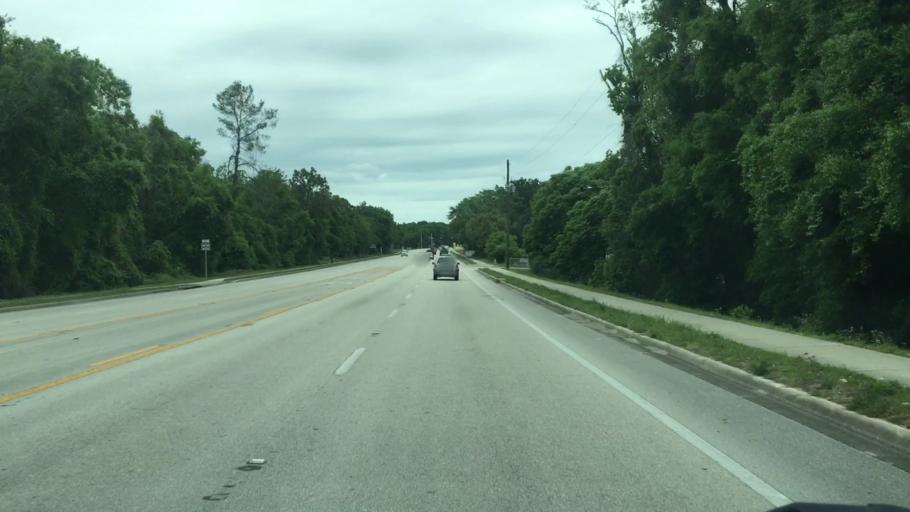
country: US
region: Florida
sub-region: Volusia County
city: De Land Southwest
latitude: 29.0094
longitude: -81.3202
